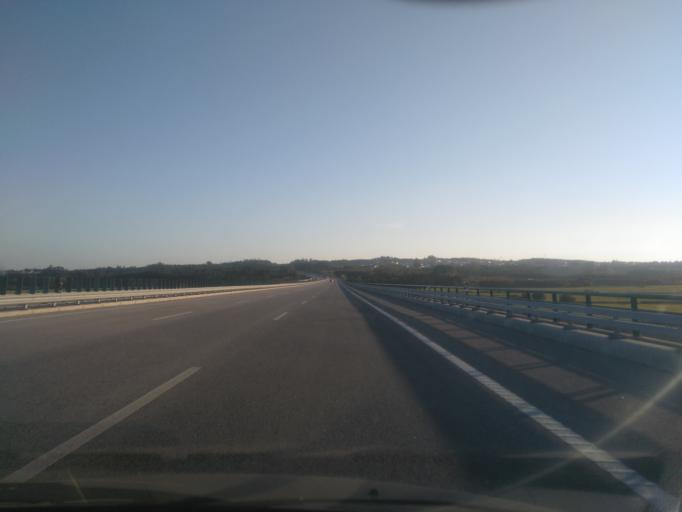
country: PT
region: Coimbra
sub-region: Figueira da Foz
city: Lavos
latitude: 40.0970
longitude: -8.7544
